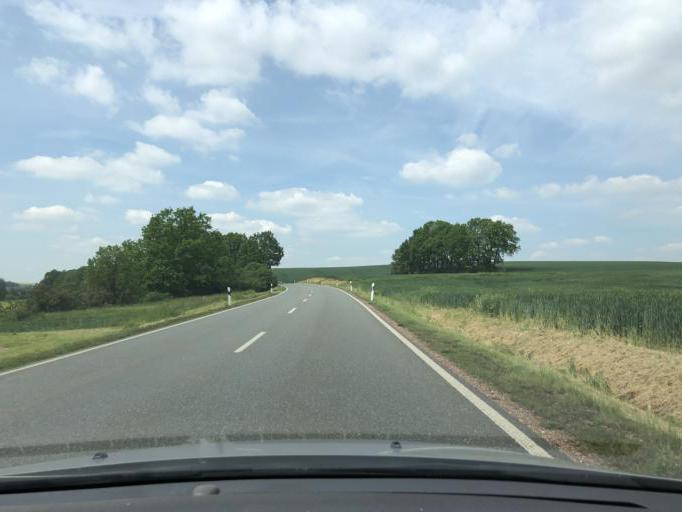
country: DE
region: Thuringia
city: Saara
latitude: 50.9260
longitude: 12.4425
